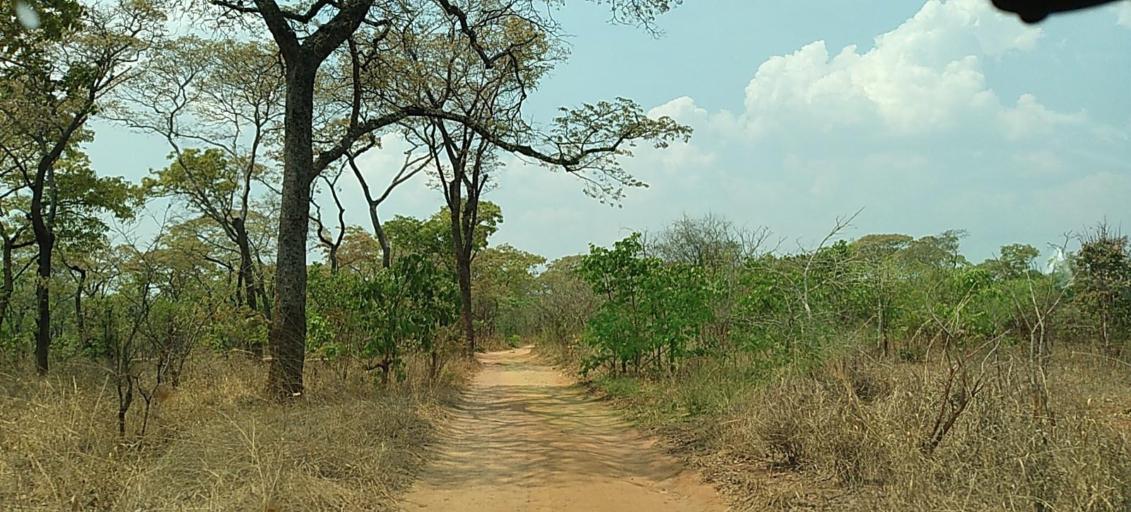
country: ZM
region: North-Western
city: Kabompo
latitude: -13.6413
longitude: 24.3814
